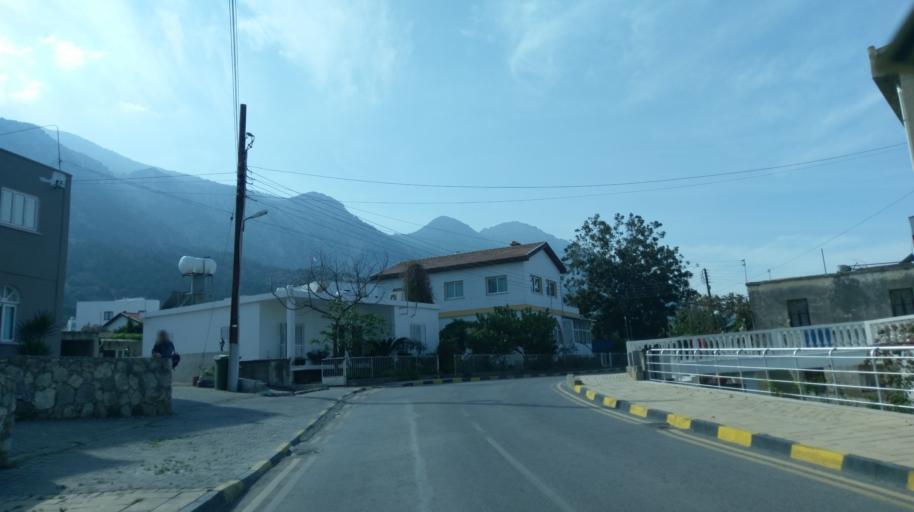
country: CY
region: Keryneia
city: Lapithos
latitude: 35.3431
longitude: 33.1714
